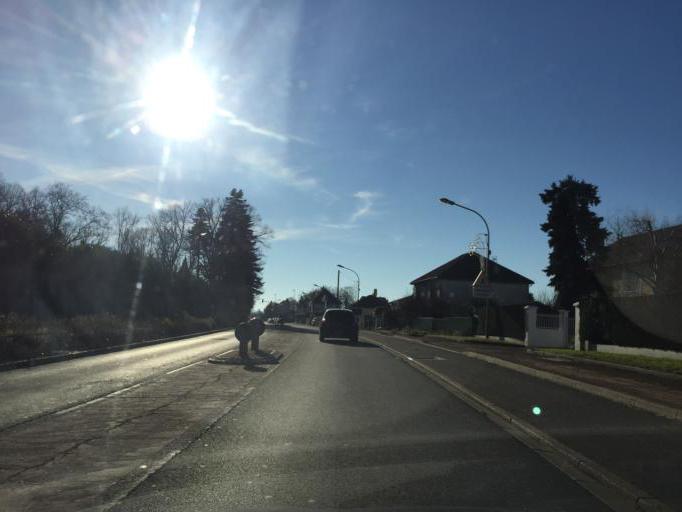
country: FR
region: Auvergne
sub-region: Departement de l'Allier
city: Saint-Remy-en-Rollat
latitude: 46.1627
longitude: 3.3930
